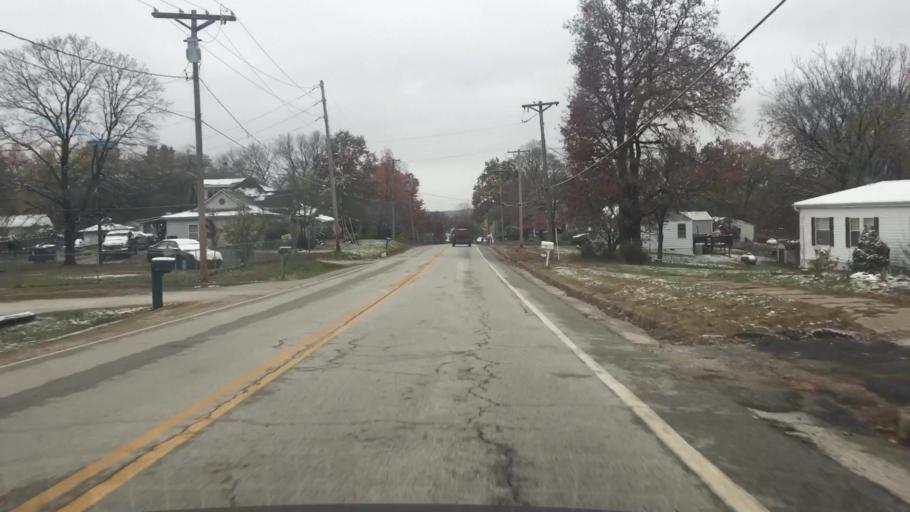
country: US
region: Missouri
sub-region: Saint Clair County
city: Osceola
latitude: 38.0398
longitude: -93.7025
